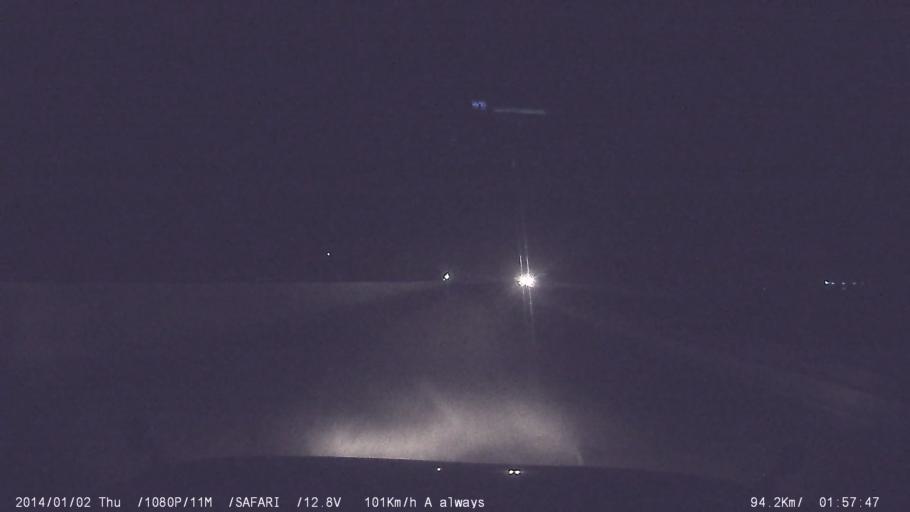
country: IN
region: Tamil Nadu
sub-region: Tiruppur
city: Uttukkuli
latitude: 11.2060
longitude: 77.3873
